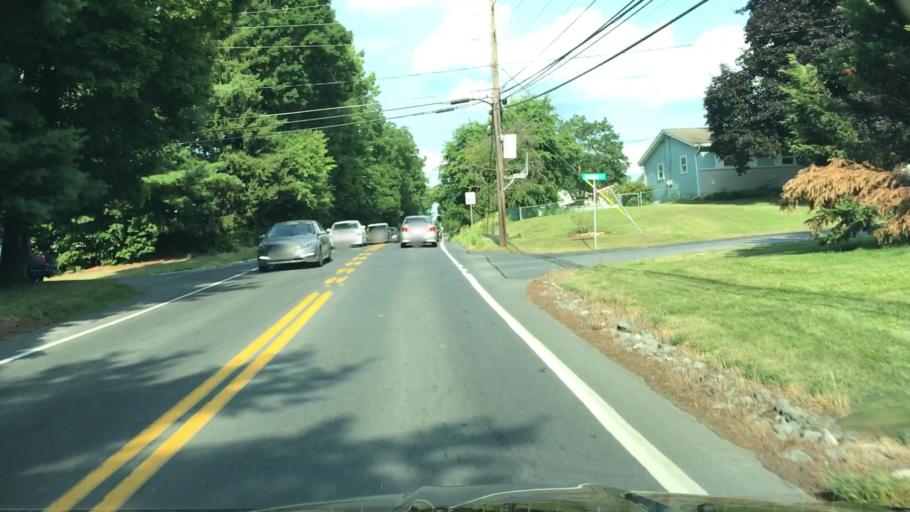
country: US
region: Pennsylvania
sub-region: Cumberland County
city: Mechanicsburg
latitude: 40.1623
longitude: -77.0110
